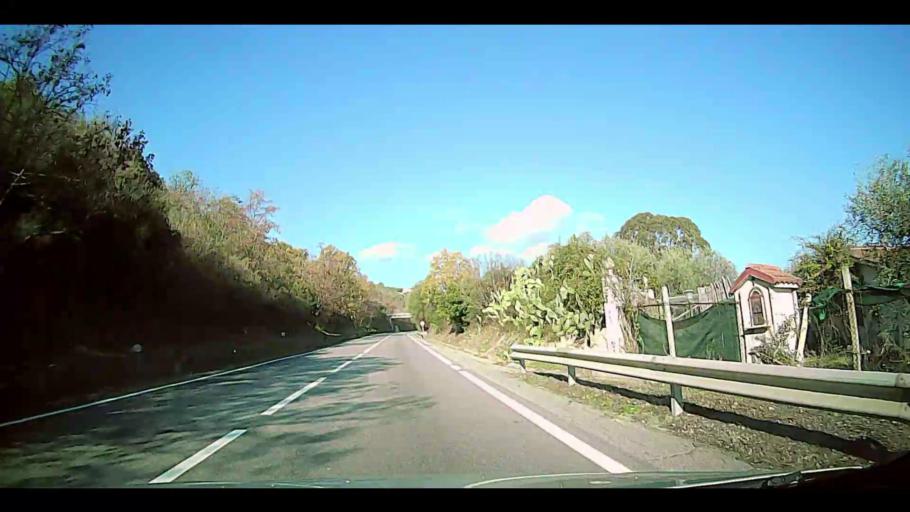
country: IT
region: Calabria
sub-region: Provincia di Crotone
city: Caccuri
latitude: 39.2030
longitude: 16.8089
